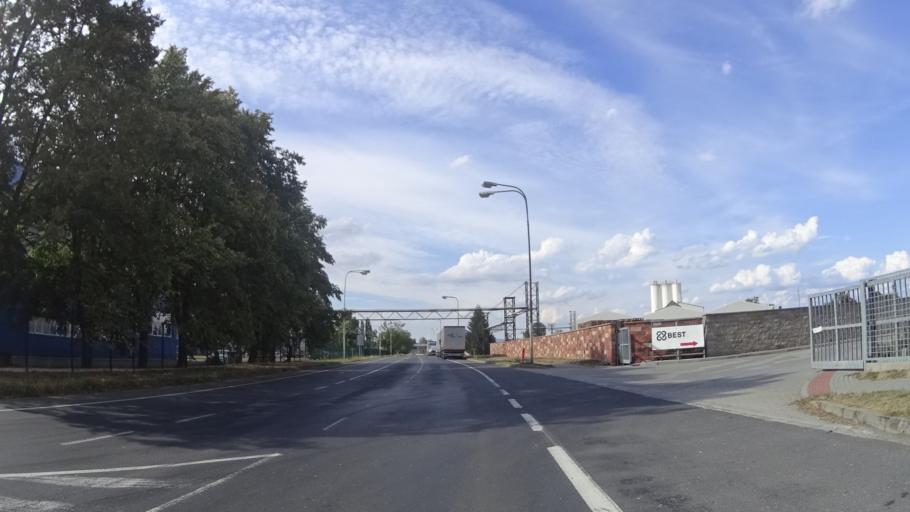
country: CZ
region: Olomoucky
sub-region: Okres Sumperk
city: Mohelnice
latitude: 49.7753
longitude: 16.9412
